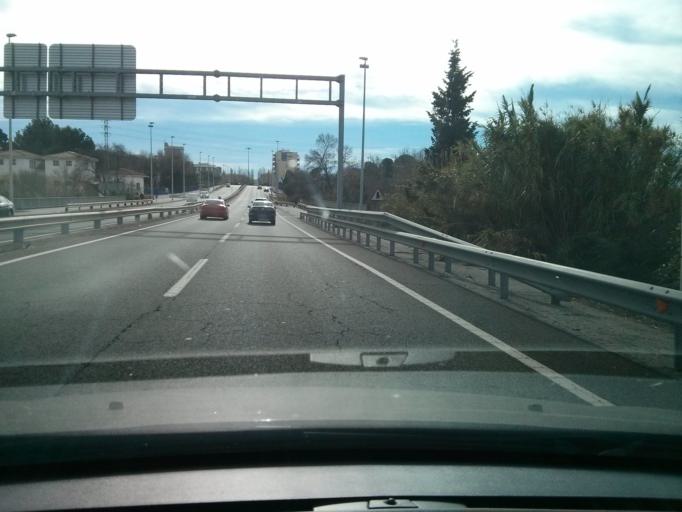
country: ES
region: Catalonia
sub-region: Provincia de Tarragona
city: Tarragona
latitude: 41.1292
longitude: 1.2408
